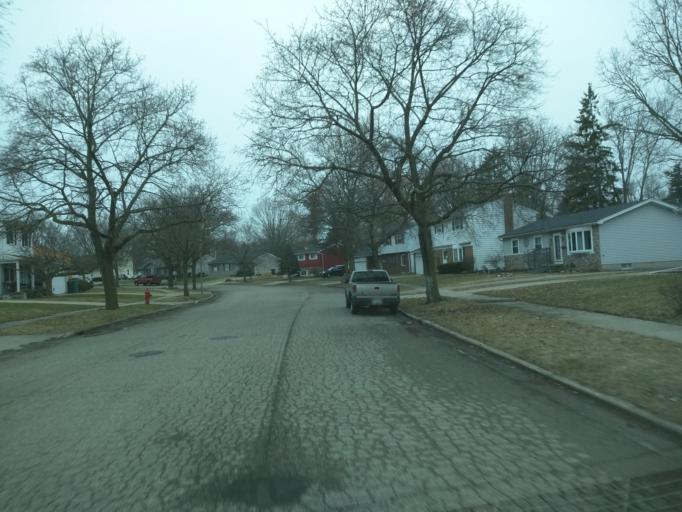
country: US
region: Michigan
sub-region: Eaton County
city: Waverly
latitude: 42.7007
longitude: -84.6021
